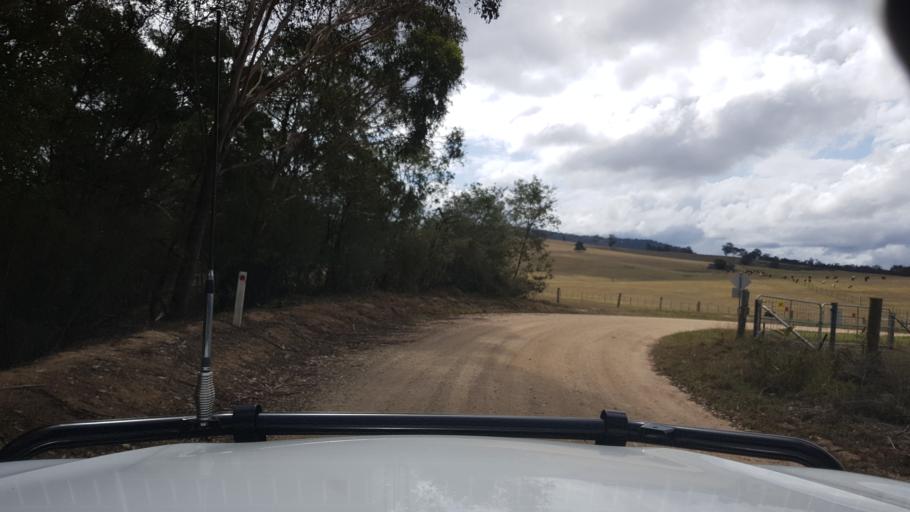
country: AU
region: Victoria
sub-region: East Gippsland
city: Bairnsdale
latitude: -37.7841
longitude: 147.5489
